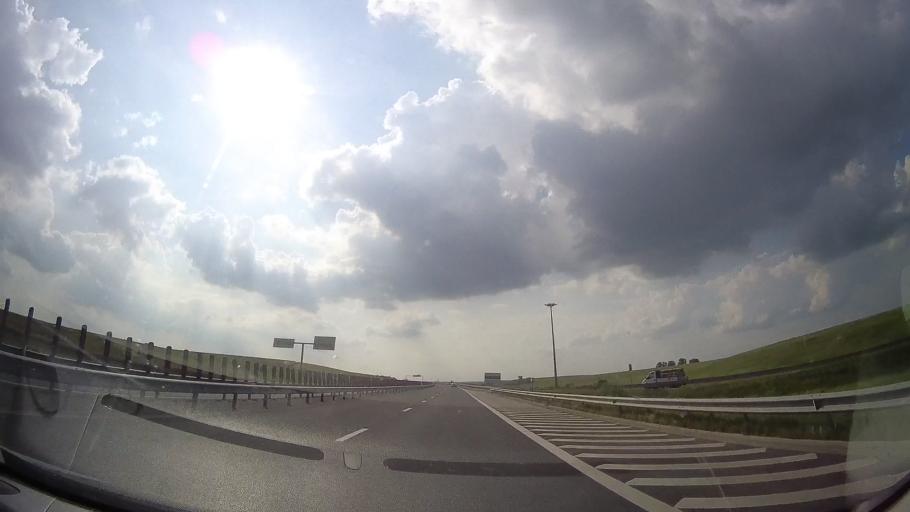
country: RO
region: Timis
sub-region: Comuna Manastiur
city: Manastiur
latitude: 45.8132
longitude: 22.0703
